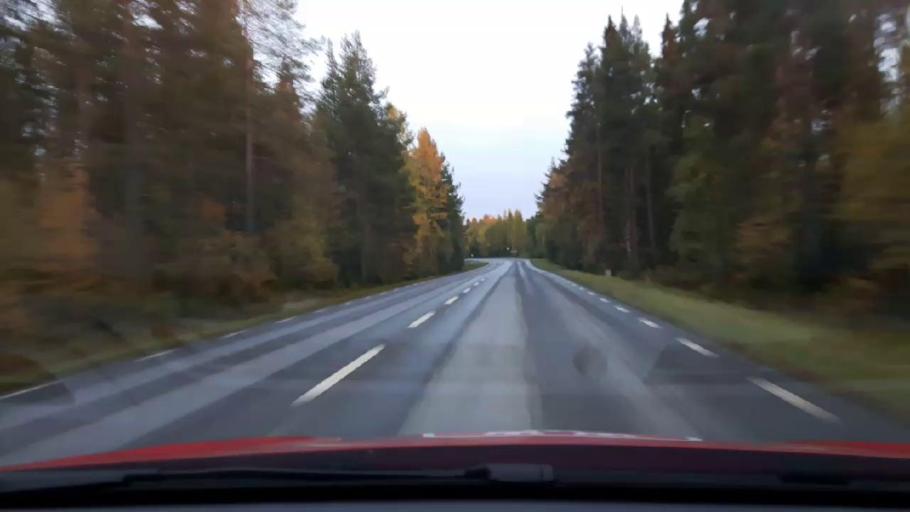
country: SE
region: Jaemtland
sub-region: OEstersunds Kommun
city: Ostersund
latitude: 63.2127
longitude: 14.6249
